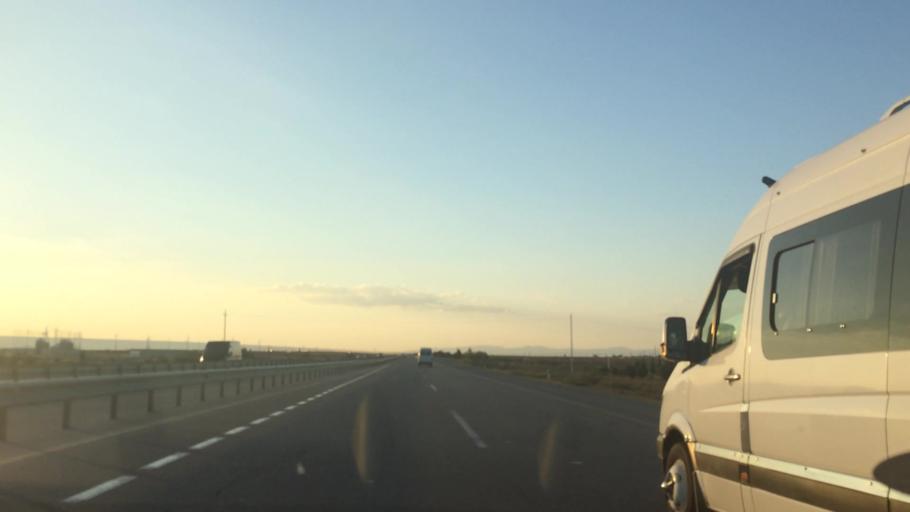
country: AZ
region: Baki
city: Qobustan
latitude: 39.9802
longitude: 49.2384
